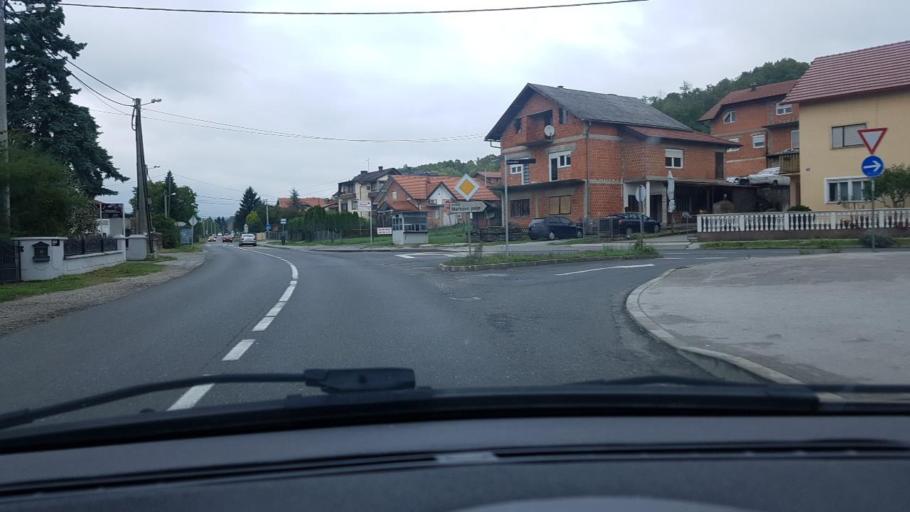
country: HR
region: Grad Zagreb
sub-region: Sesvete
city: Sesvete
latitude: 45.8620
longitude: 16.1149
